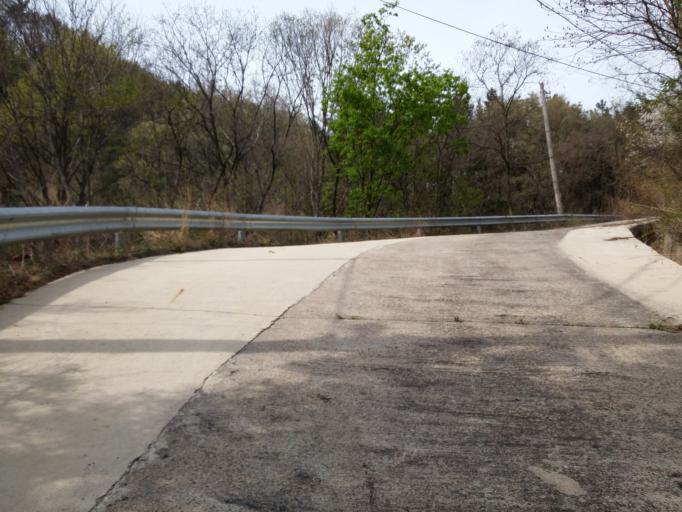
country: KR
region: Chungcheongbuk-do
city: Okcheon
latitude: 36.2571
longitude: 127.5582
